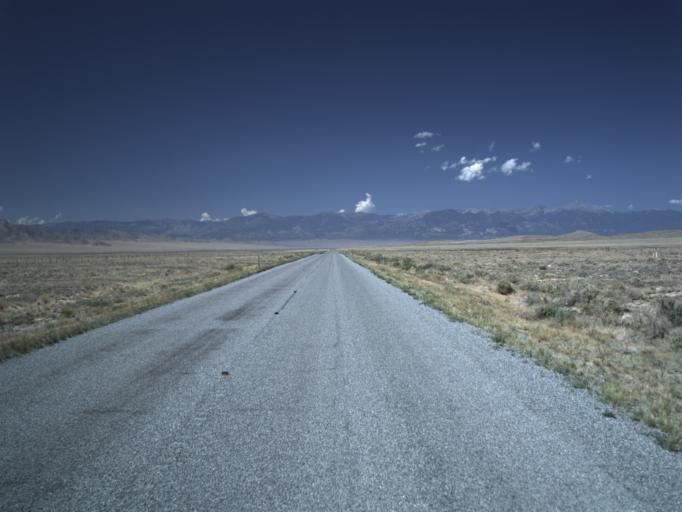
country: US
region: Utah
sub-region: Beaver County
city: Milford
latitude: 39.0591
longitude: -113.7600
